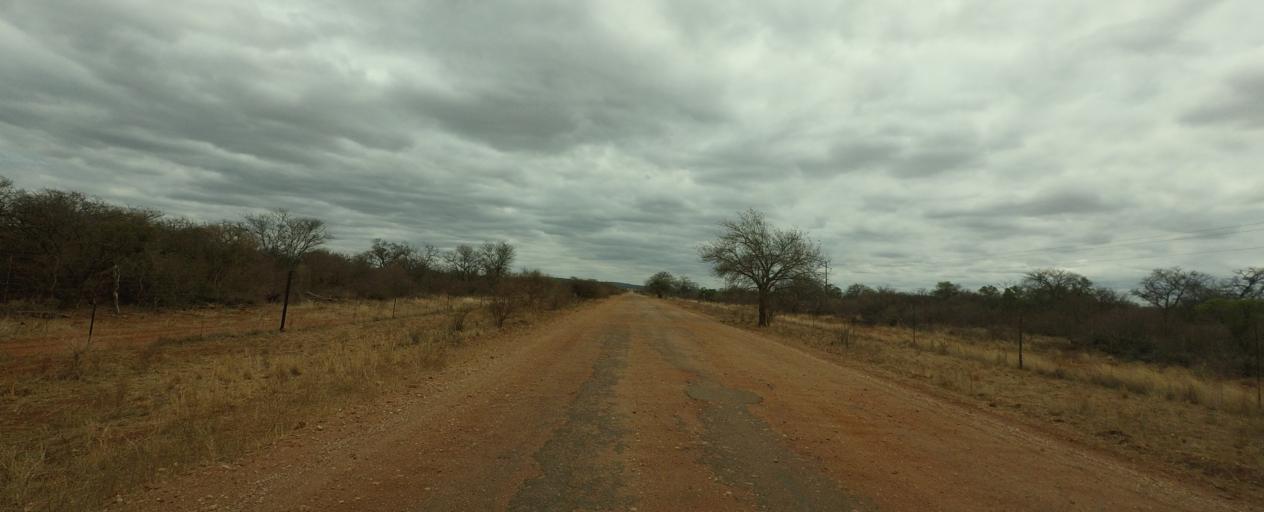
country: BW
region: Central
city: Mathathane
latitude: -22.7402
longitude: 28.4889
